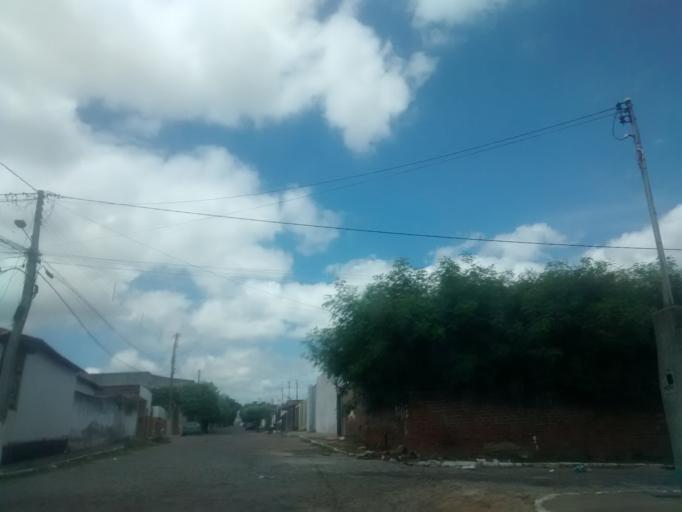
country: BR
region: Bahia
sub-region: Brumado
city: Brumado
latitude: -14.2001
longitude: -41.6706
